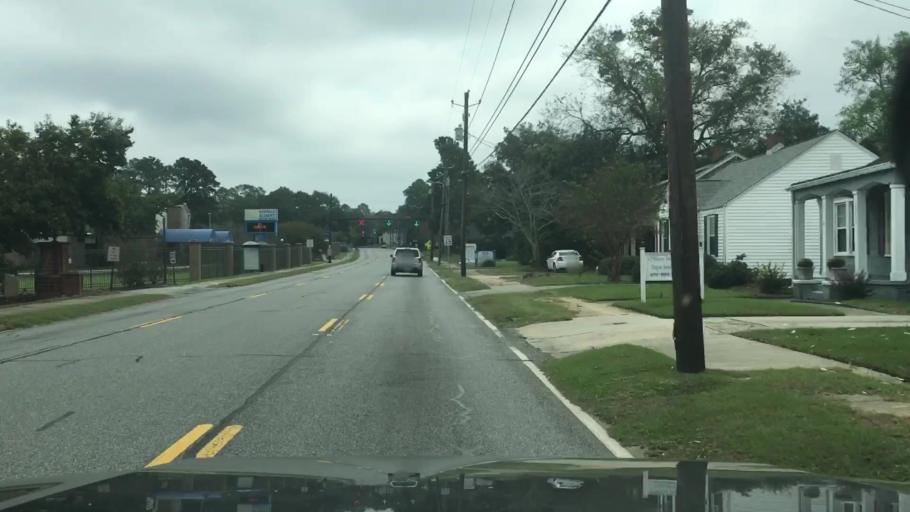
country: US
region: Georgia
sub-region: Bibb County
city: Macon
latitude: 32.8476
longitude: -83.6704
